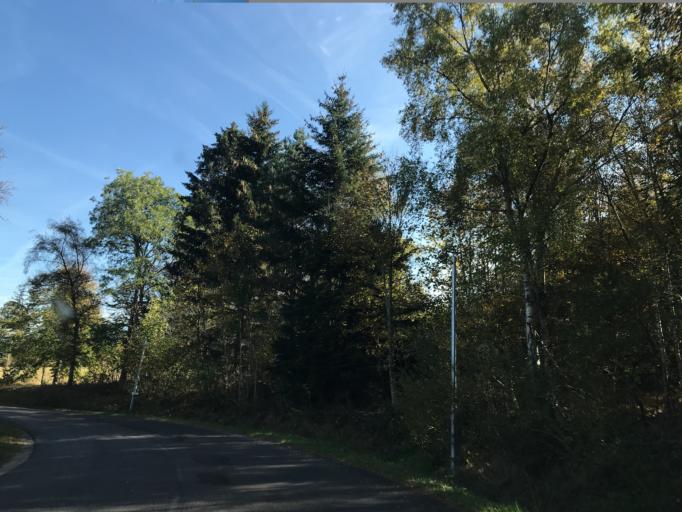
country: FR
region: Rhone-Alpes
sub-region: Departement de la Loire
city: Noiretable
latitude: 45.8061
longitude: 3.7320
